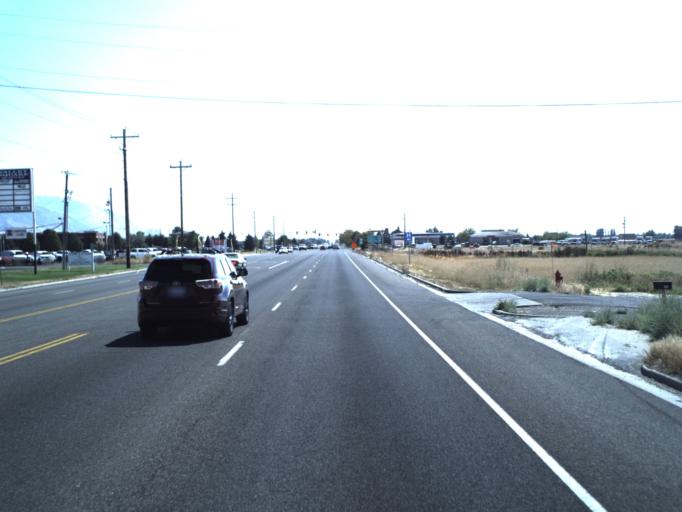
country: US
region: Utah
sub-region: Cache County
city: Hyde Park
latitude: 41.7811
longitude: -111.8340
